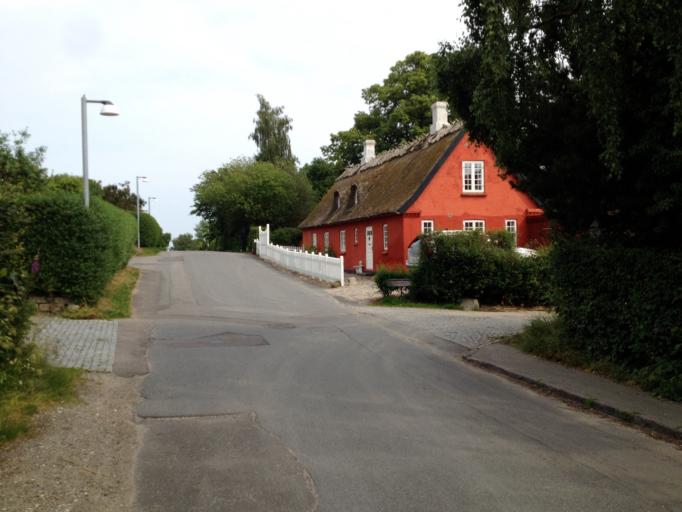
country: DK
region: Capital Region
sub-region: Fredensborg Kommune
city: Humlebaek
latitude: 55.9528
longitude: 12.5277
